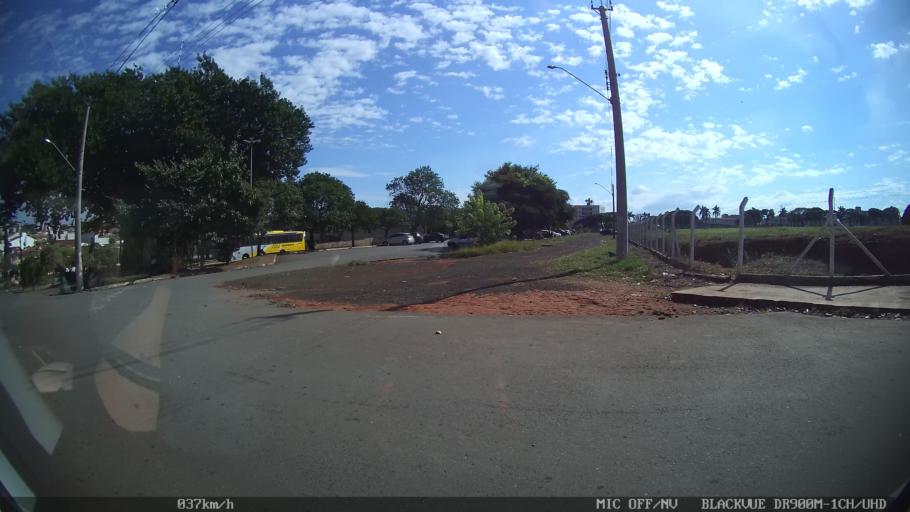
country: BR
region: Sao Paulo
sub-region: Americana
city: Americana
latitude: -22.7348
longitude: -47.3095
